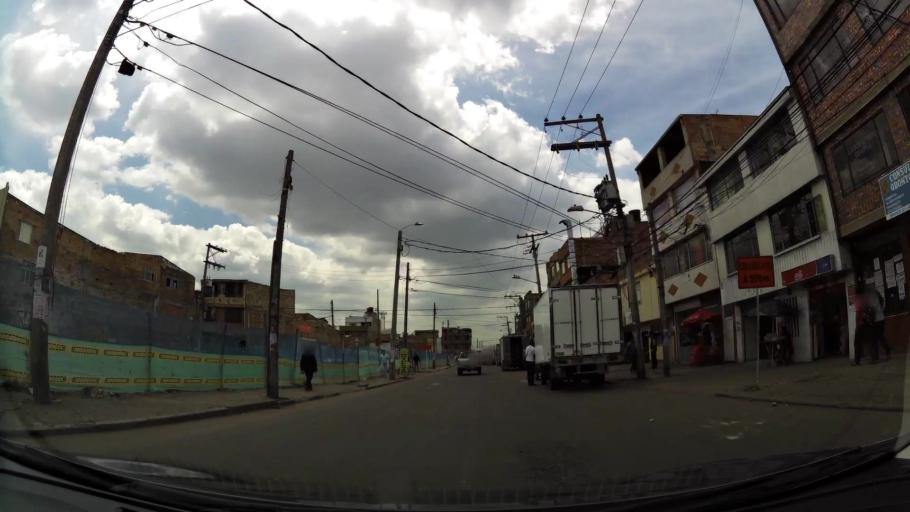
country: CO
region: Cundinamarca
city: Cota
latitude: 4.7313
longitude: -74.0885
